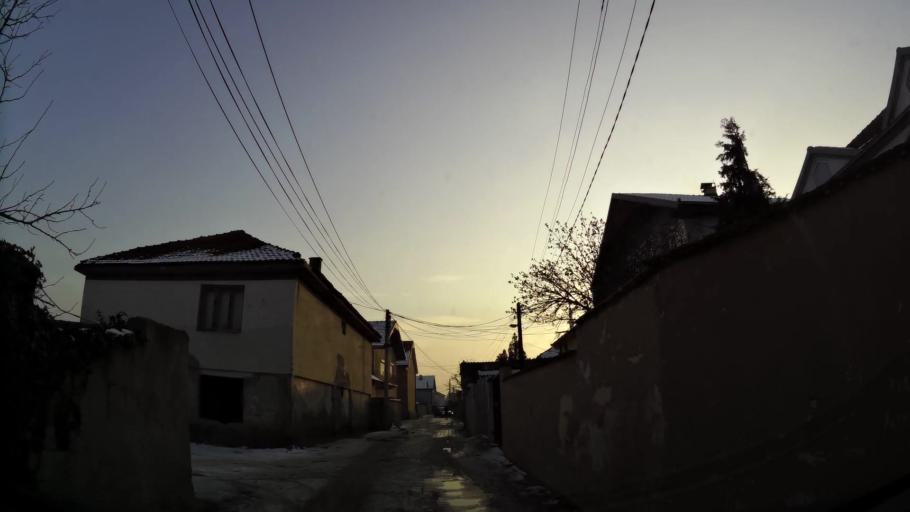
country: MK
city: Creshevo
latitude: 42.0163
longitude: 21.5155
